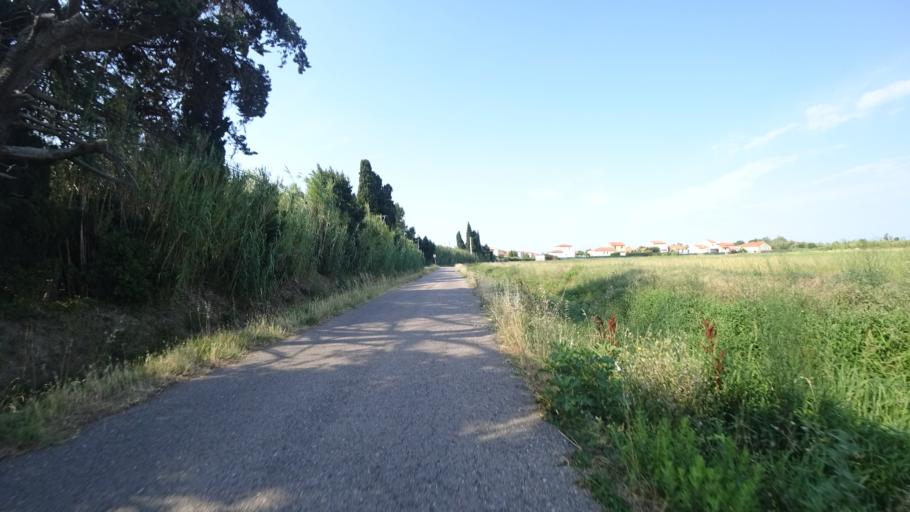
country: FR
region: Languedoc-Roussillon
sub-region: Departement des Pyrenees-Orientales
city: Saint-Laurent-de-la-Salanque
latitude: 42.7818
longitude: 2.9987
